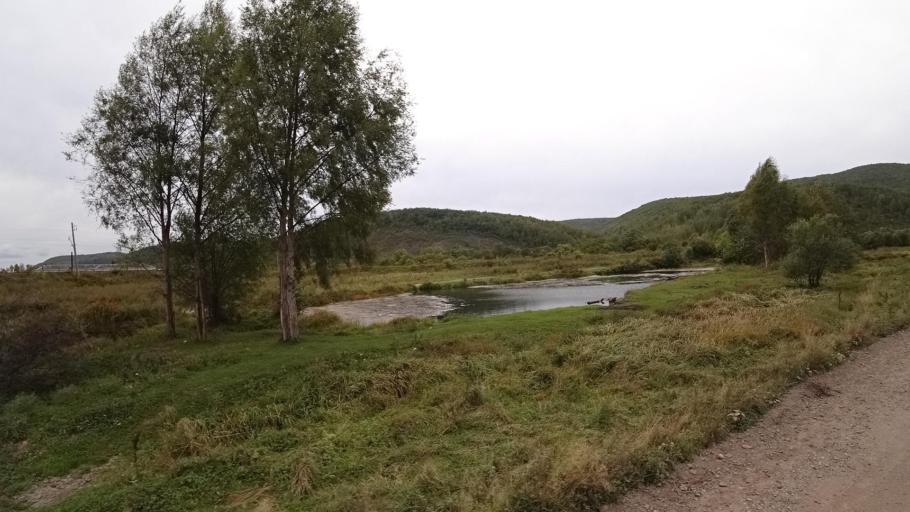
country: RU
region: Jewish Autonomous Oblast
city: Khingansk
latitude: 49.0312
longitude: 131.0491
